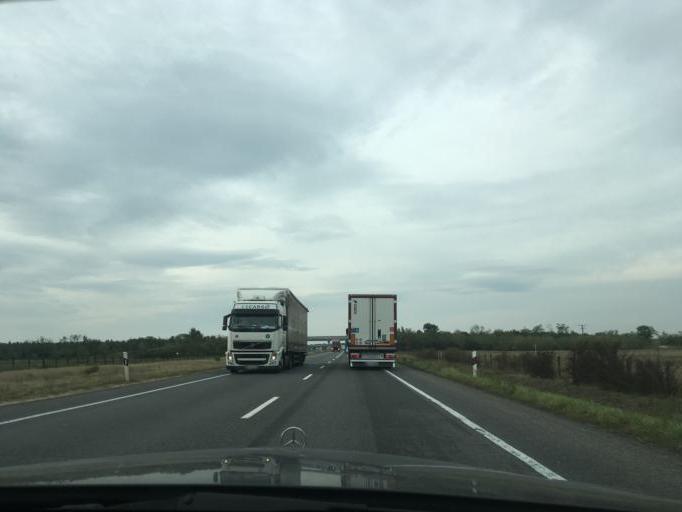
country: HU
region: Gyor-Moson-Sopron
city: Rajka
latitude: 47.9639
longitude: 17.1725
